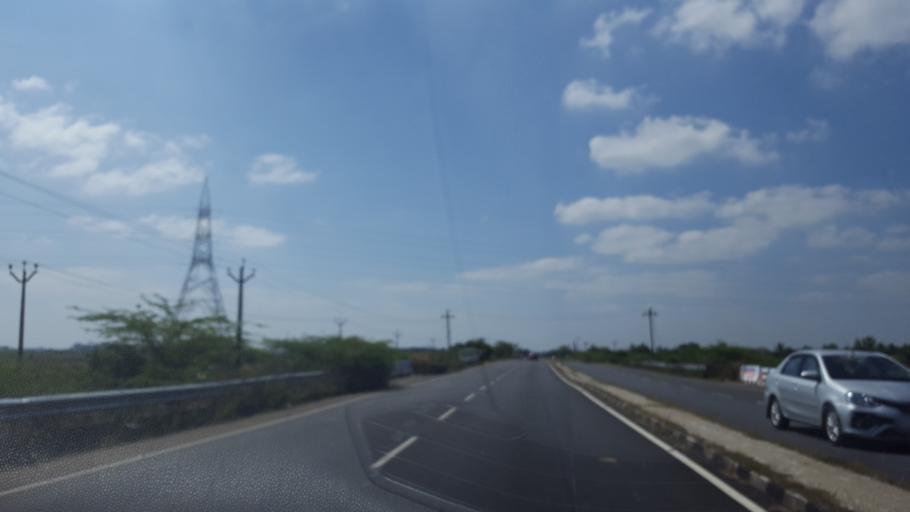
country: IN
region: Tamil Nadu
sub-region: Kancheepuram
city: Mamallapuram
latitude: 12.6669
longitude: 80.1781
